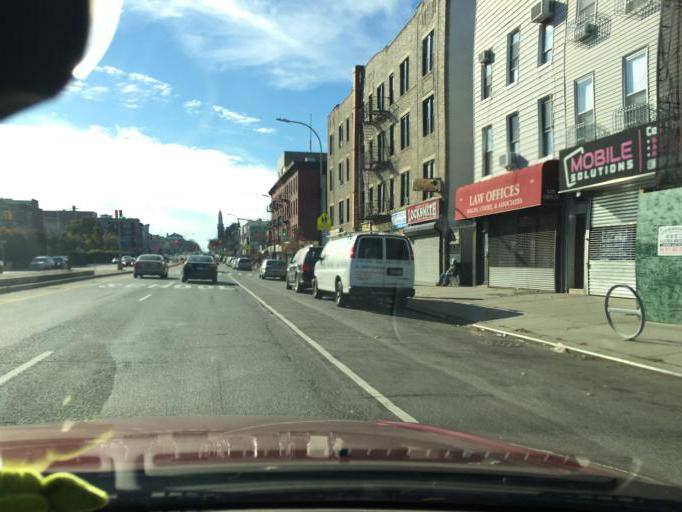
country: US
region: New York
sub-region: Kings County
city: Brooklyn
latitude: 40.6560
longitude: -74.0029
